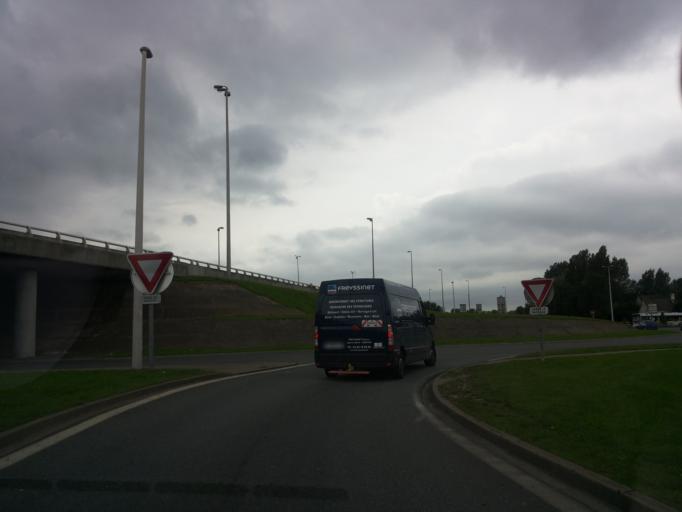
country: FR
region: Nord-Pas-de-Calais
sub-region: Departement du Pas-de-Calais
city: Coulogne
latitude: 50.9344
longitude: 1.8918
